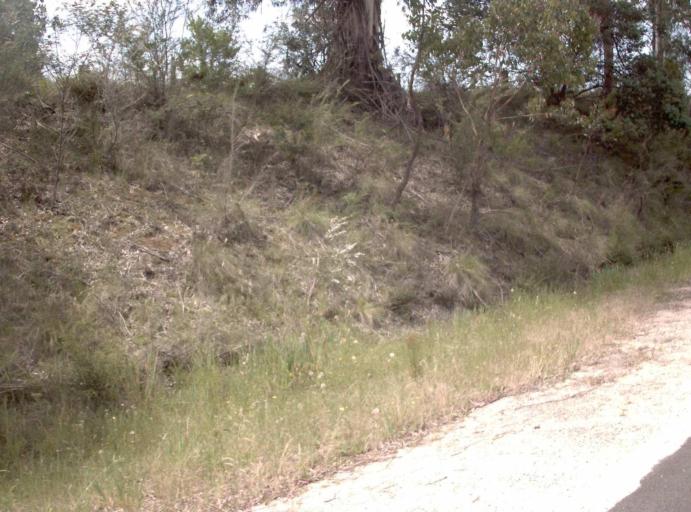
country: AU
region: New South Wales
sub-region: Bega Valley
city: Eden
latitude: -37.5451
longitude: 149.4538
